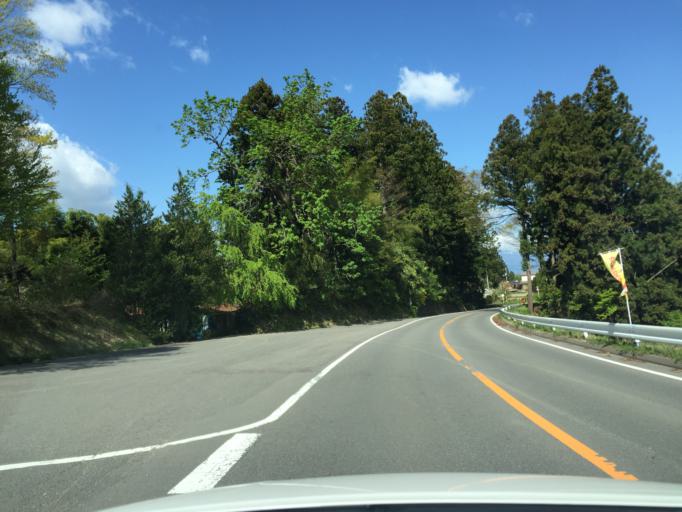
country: JP
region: Fukushima
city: Funehikimachi-funehiki
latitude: 37.5385
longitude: 140.5787
